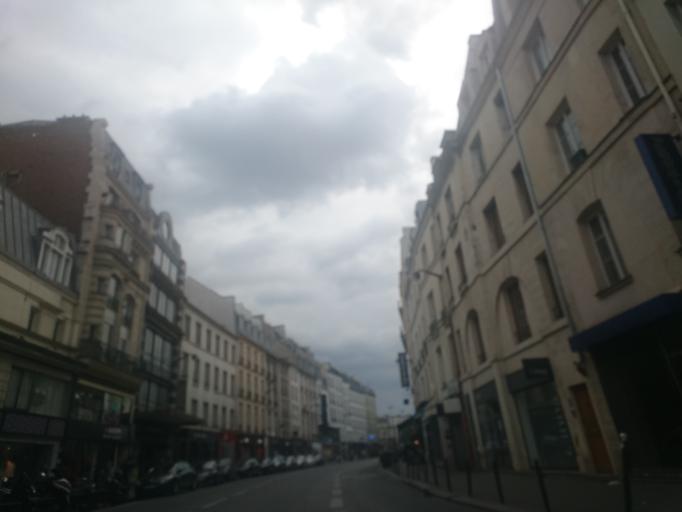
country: FR
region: Ile-de-France
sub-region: Paris
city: Paris
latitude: 48.8524
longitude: 2.3721
